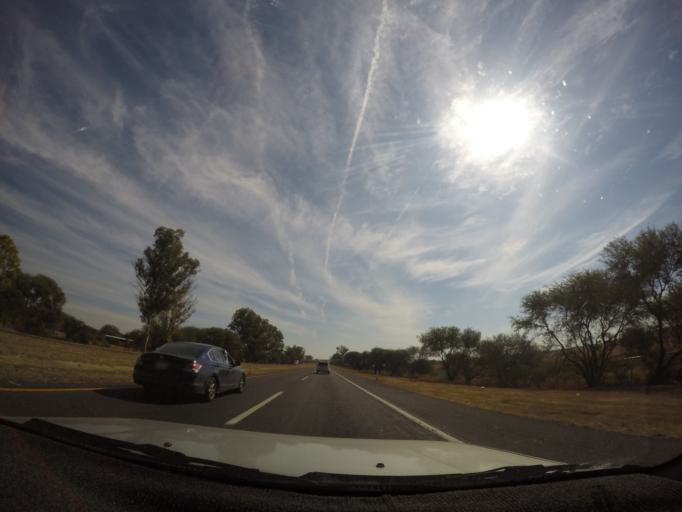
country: MX
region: Jalisco
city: La Barca
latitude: 20.3220
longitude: -102.5430
